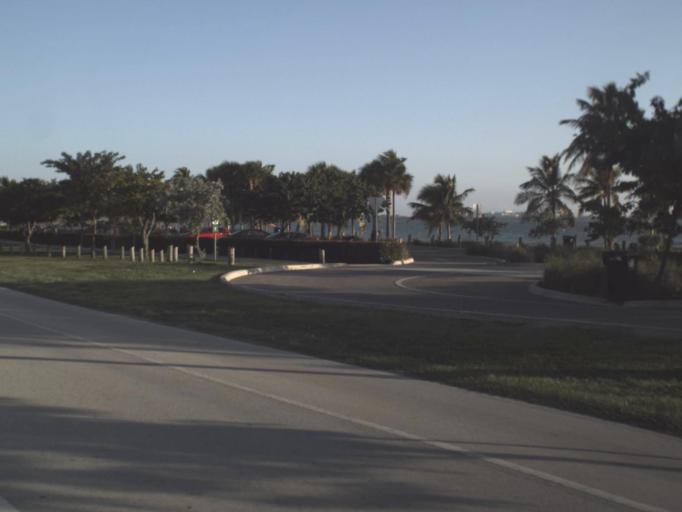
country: US
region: Florida
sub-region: Miami-Dade County
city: Miami
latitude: 25.7461
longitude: -80.1767
